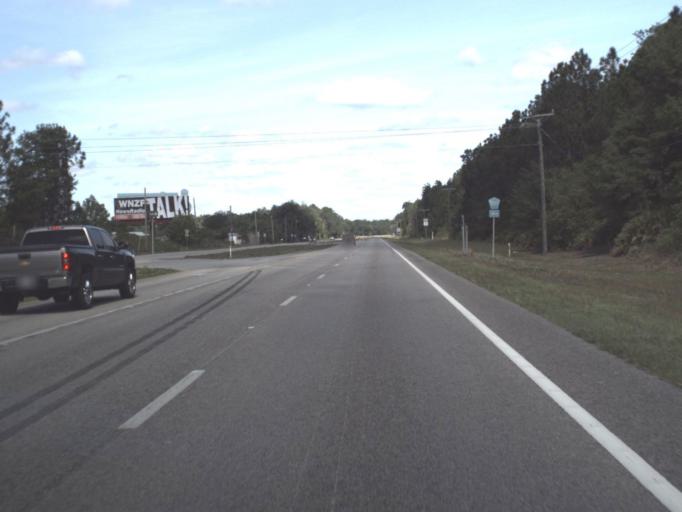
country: US
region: Florida
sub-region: Flagler County
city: Bunnell
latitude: 29.4271
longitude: -81.2226
